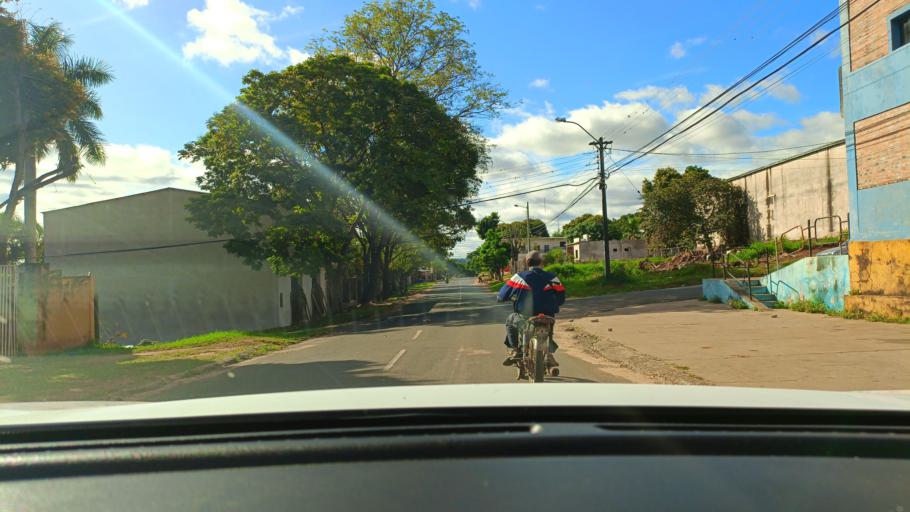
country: PY
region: San Pedro
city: Guayaybi
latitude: -24.6716
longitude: -56.4468
